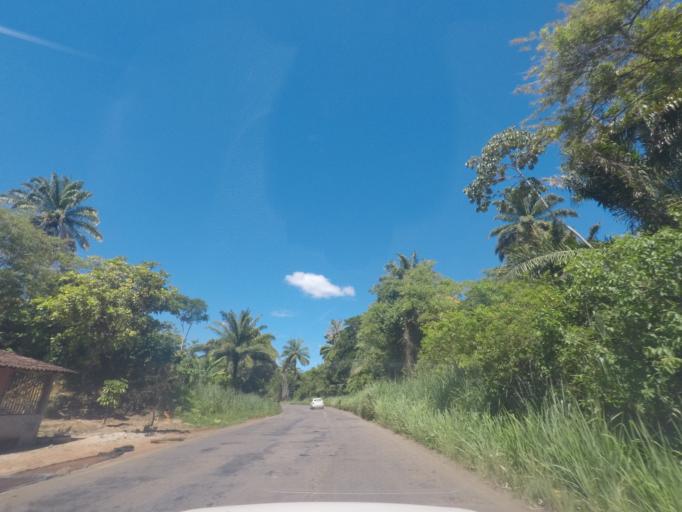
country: BR
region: Bahia
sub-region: Taperoa
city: Taperoa
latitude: -13.4943
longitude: -39.0941
